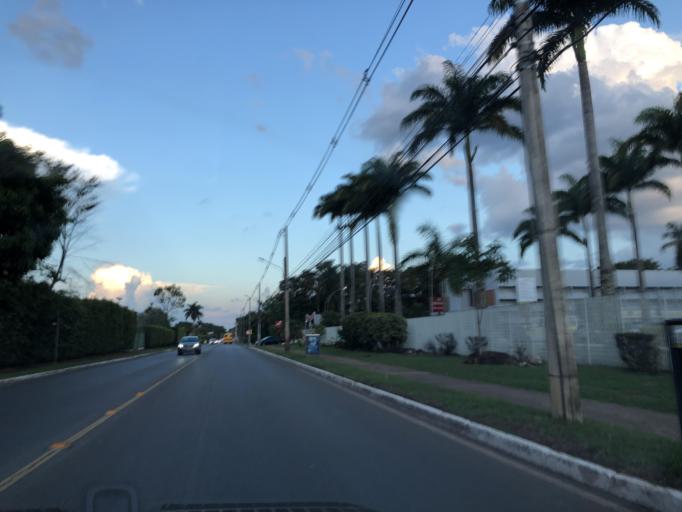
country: BR
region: Federal District
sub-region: Brasilia
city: Brasilia
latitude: -15.8499
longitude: -47.8965
